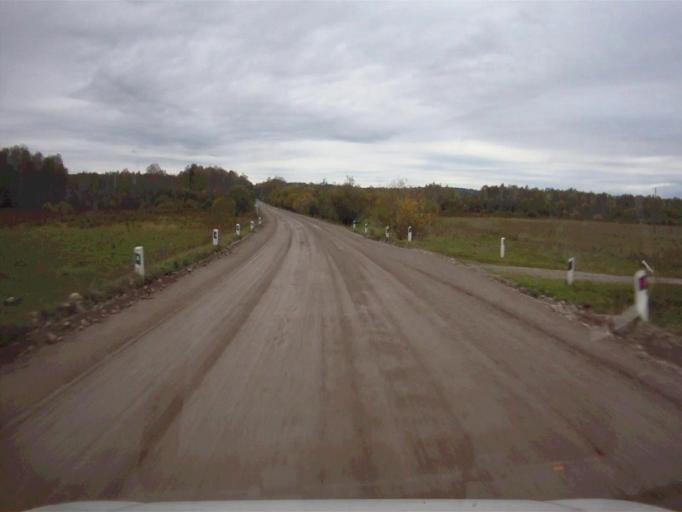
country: RU
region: Chelyabinsk
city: Nyazepetrovsk
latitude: 56.1255
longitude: 59.3521
